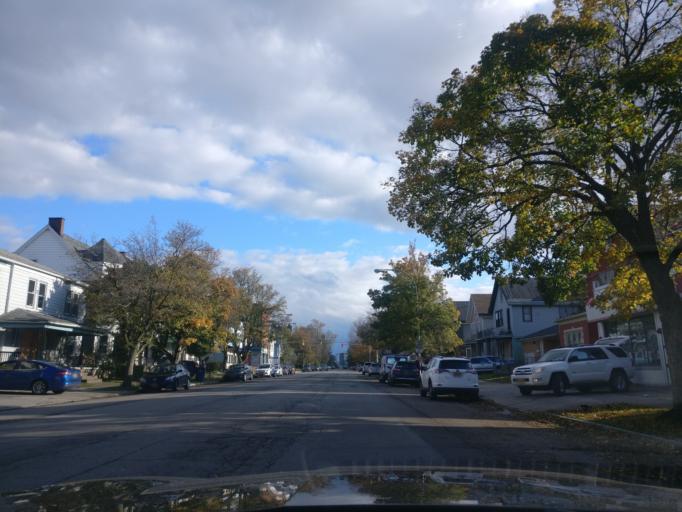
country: US
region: New York
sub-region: Erie County
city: Buffalo
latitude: 42.9068
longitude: -78.8974
